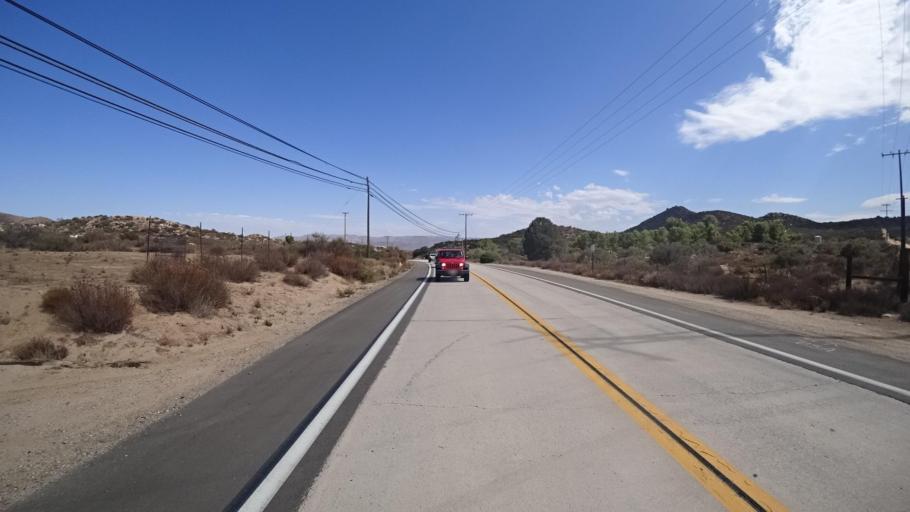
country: MX
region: Baja California
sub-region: Tecate
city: Cereso del Hongo
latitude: 32.6440
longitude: -116.2343
